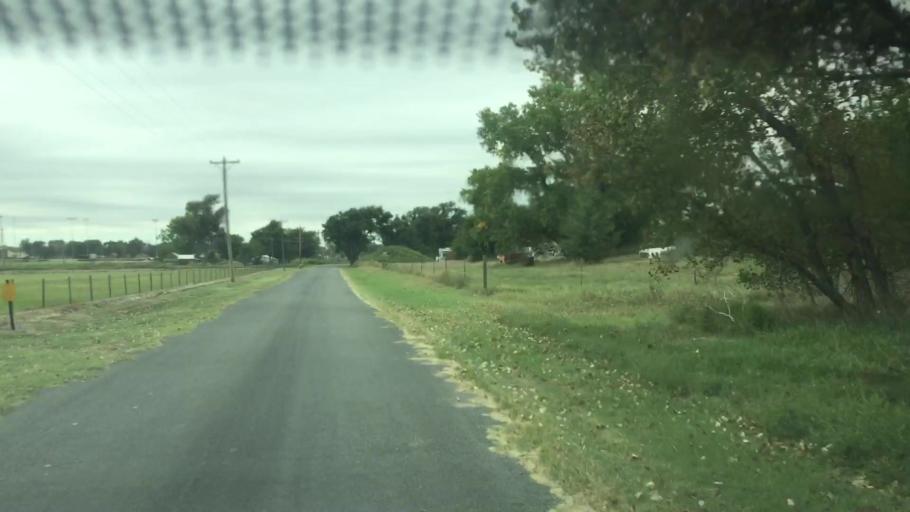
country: US
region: Kansas
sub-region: Hamilton County
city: Syracuse
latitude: 38.0572
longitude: -102.1140
